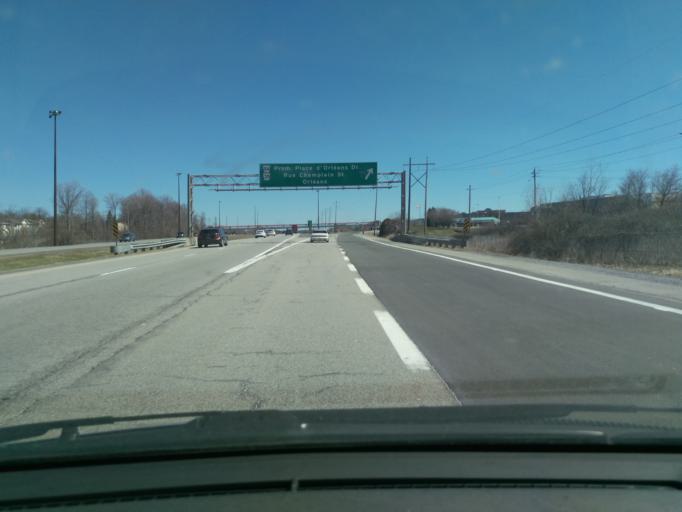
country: CA
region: Quebec
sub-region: Outaouais
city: Gatineau
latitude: 45.4767
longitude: -75.5256
